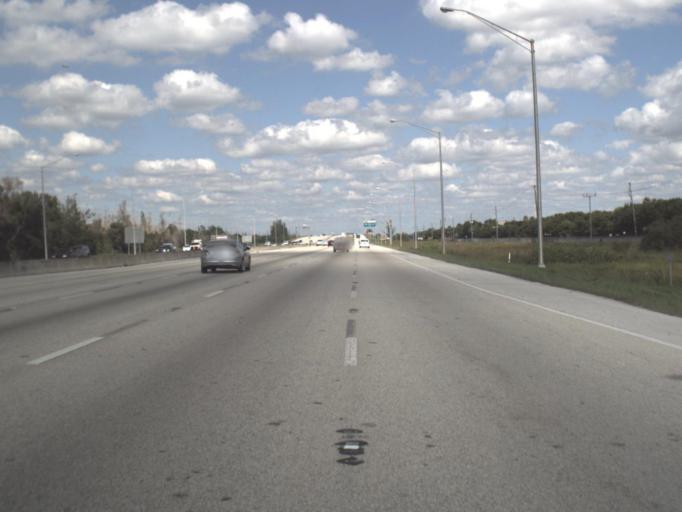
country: US
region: Florida
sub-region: Miami-Dade County
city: Doral
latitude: 25.8183
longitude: -80.3864
